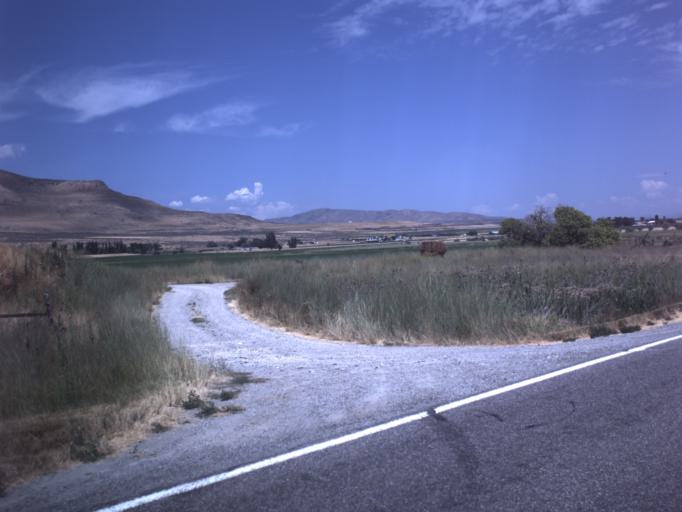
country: US
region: Utah
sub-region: Box Elder County
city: Tremonton
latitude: 41.6366
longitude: -112.3288
